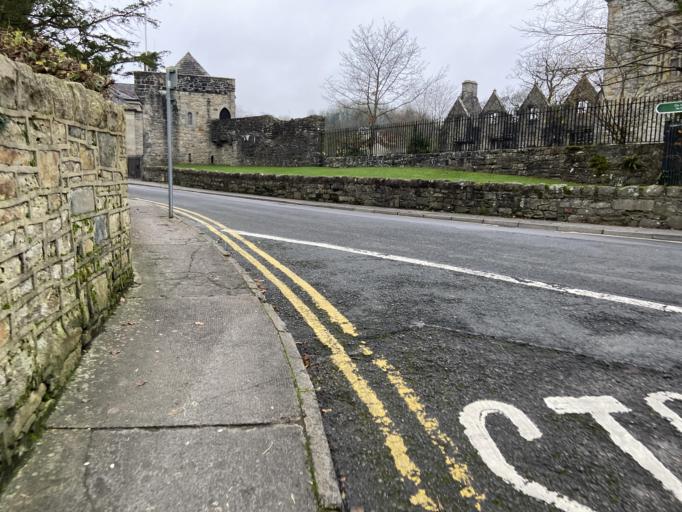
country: IE
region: Ulster
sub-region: County Donegal
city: Donegal
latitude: 54.6550
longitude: -8.1099
